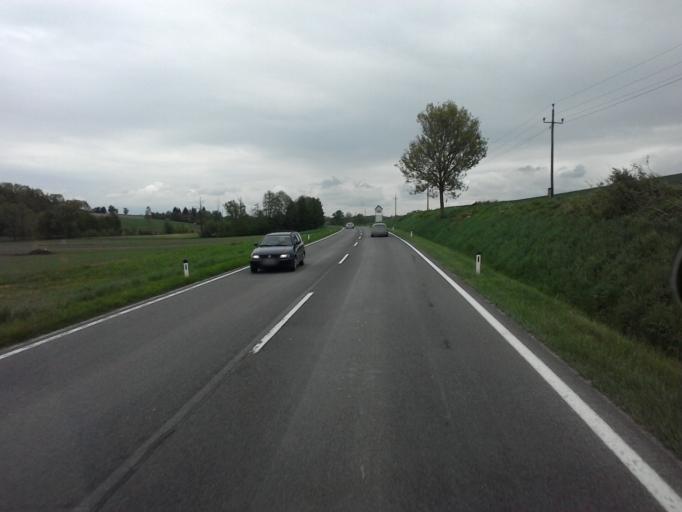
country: AT
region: Upper Austria
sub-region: Politischer Bezirk Vocklabruck
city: Wolfsegg am Hausruck
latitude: 48.2194
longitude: 13.7105
